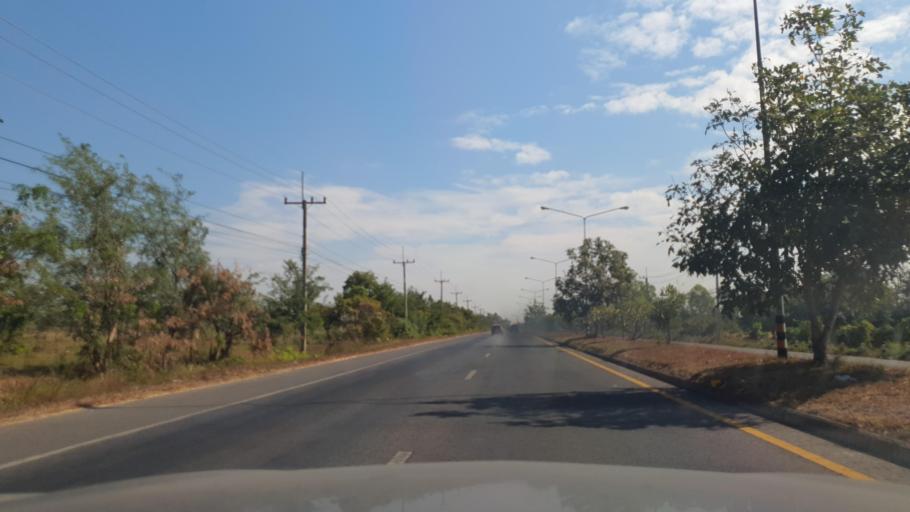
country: TH
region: Maha Sarakham
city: Kantharawichai
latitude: 16.3838
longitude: 103.2241
